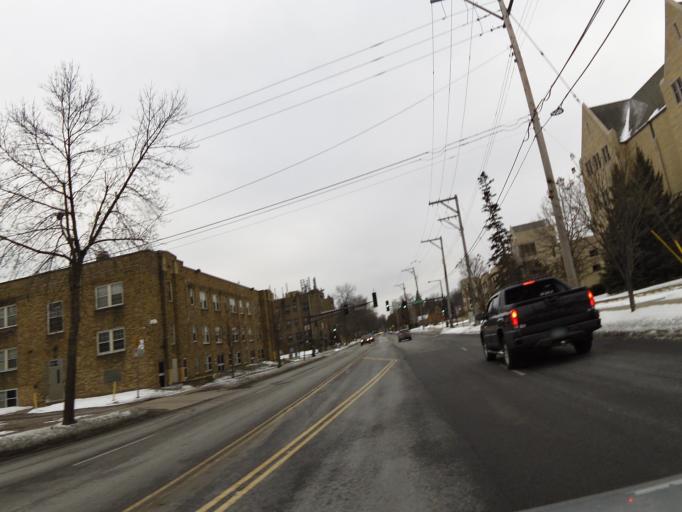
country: US
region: Minnesota
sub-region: Ramsey County
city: Falcon Heights
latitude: 44.9410
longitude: -93.1925
